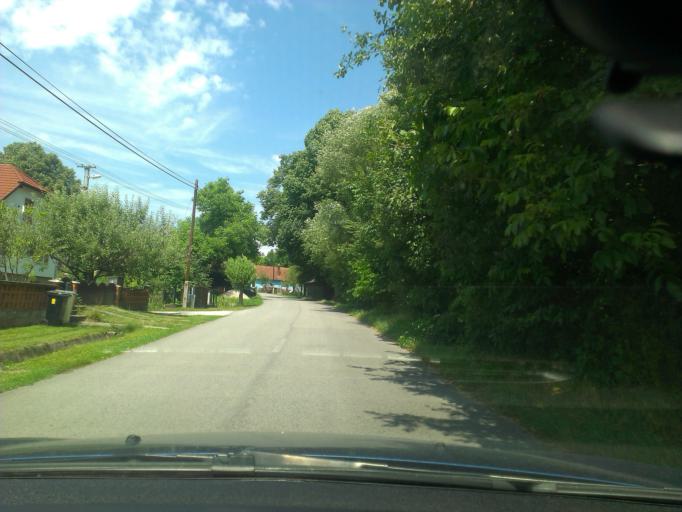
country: SK
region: Trenciansky
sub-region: Okres Myjava
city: Myjava
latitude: 48.7890
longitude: 17.5654
